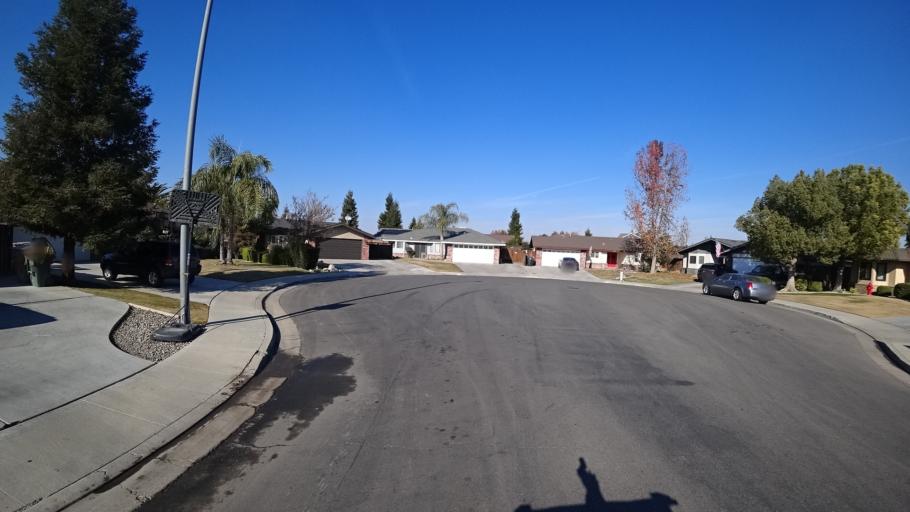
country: US
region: California
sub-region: Kern County
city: Greenfield
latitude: 35.2989
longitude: -119.0440
